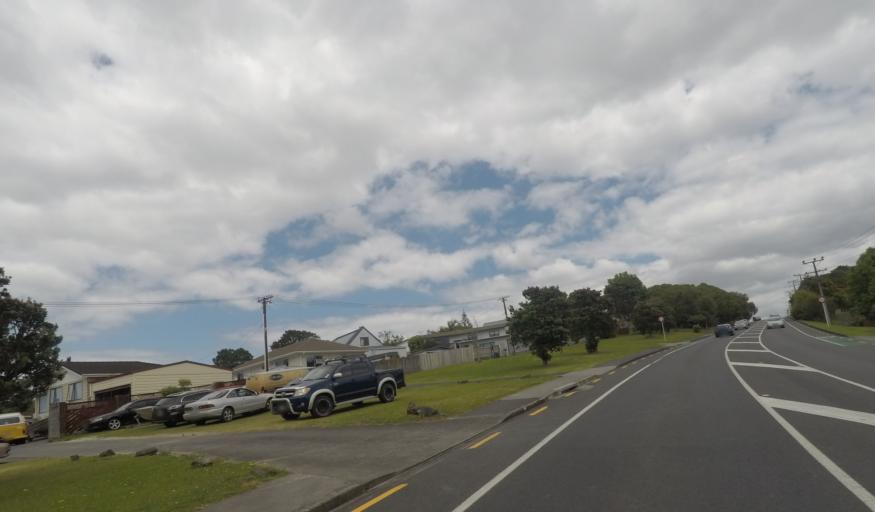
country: NZ
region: Auckland
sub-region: Auckland
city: Rosebank
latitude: -36.8288
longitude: 174.6076
